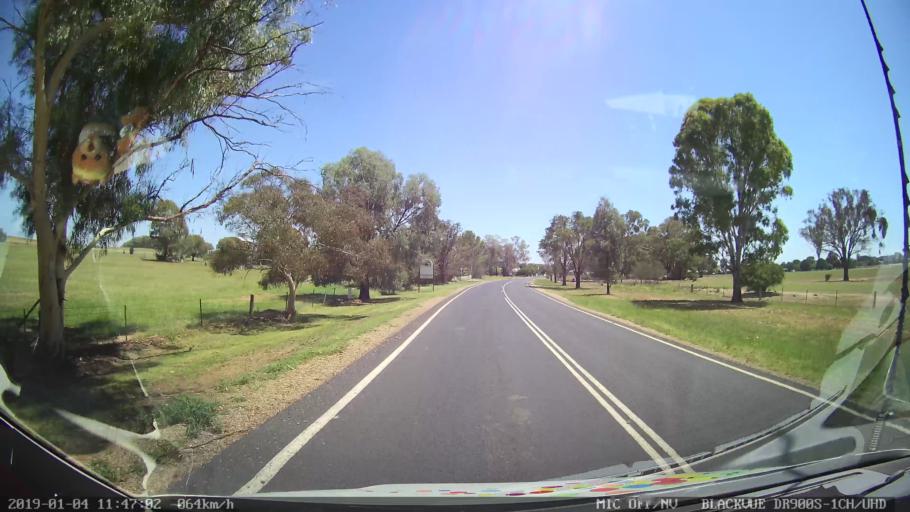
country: AU
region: New South Wales
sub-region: Cabonne
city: Molong
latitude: -32.9360
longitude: 148.7558
